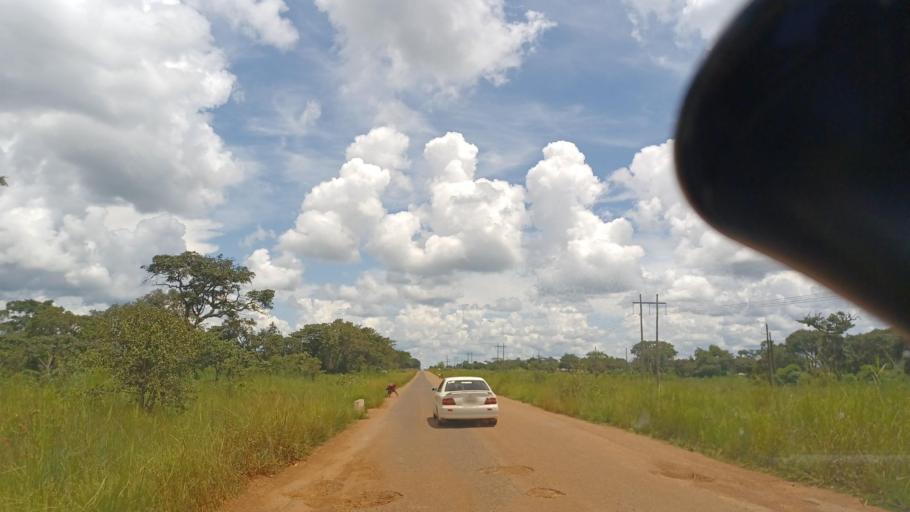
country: ZM
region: North-Western
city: Solwezi
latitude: -12.4847
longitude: 26.1953
